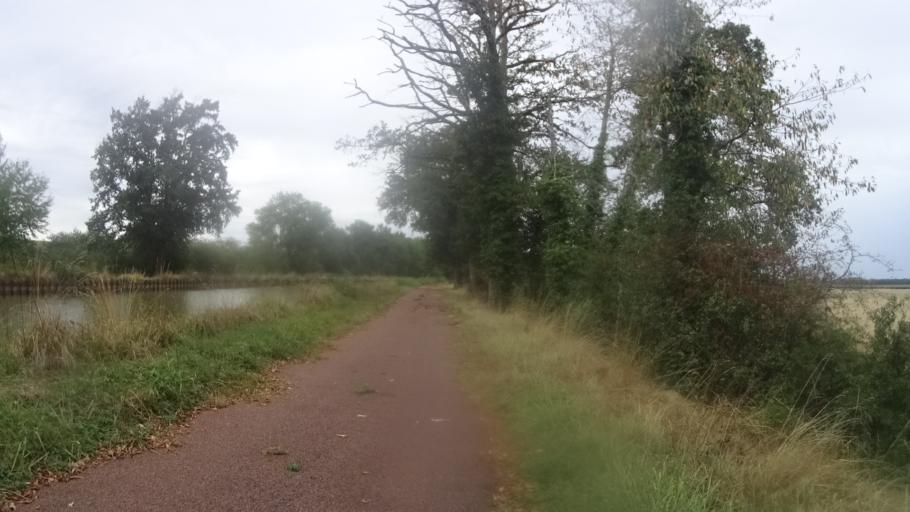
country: FR
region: Bourgogne
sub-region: Departement de la Nievre
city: Imphy
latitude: 46.8653
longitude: 3.2837
